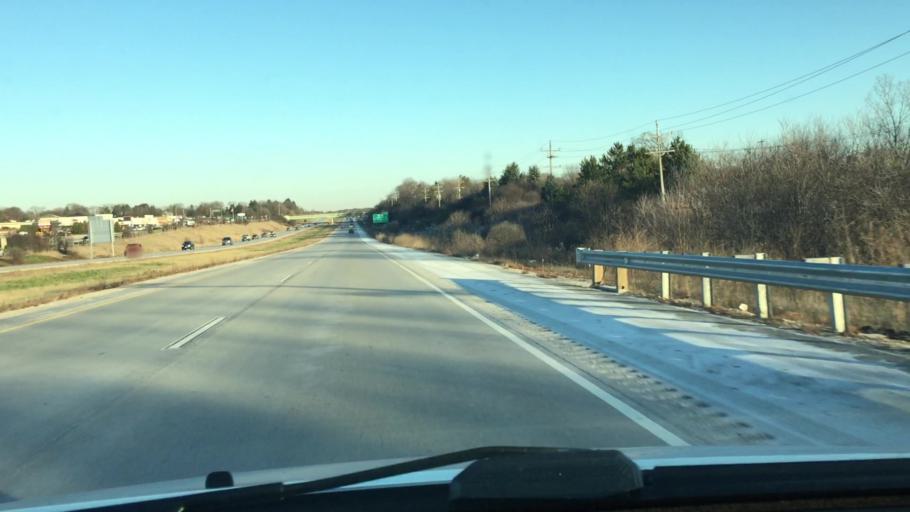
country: US
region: Wisconsin
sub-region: Waukesha County
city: Hartland
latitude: 43.1096
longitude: -88.3428
